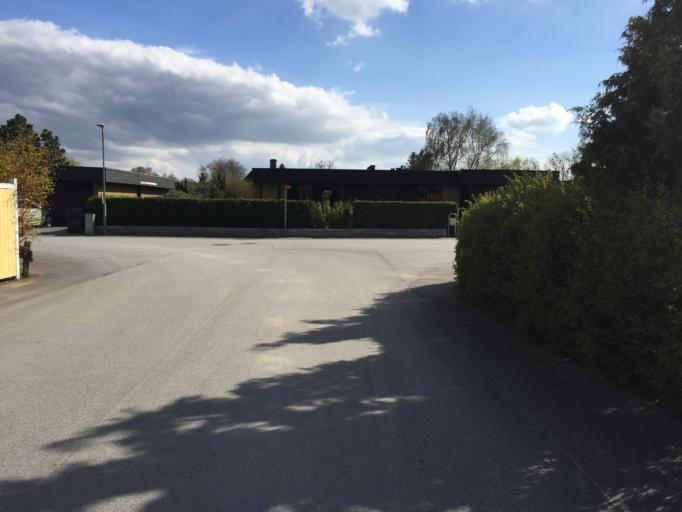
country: SE
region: Skane
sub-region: Lunds Kommun
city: Veberod
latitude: 55.6299
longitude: 13.4973
